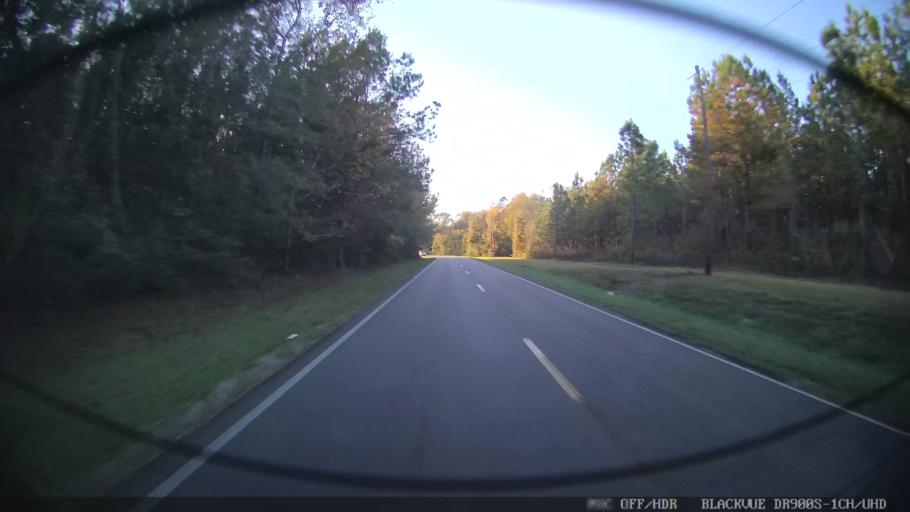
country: US
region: Mississippi
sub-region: Lamar County
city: Lumberton
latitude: 31.0001
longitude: -89.4116
